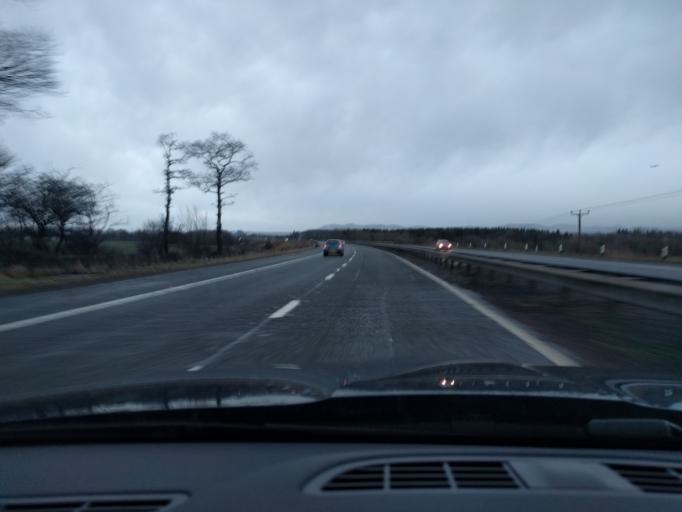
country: GB
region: Scotland
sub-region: Edinburgh
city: Kirkliston
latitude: 55.9594
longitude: -3.4386
